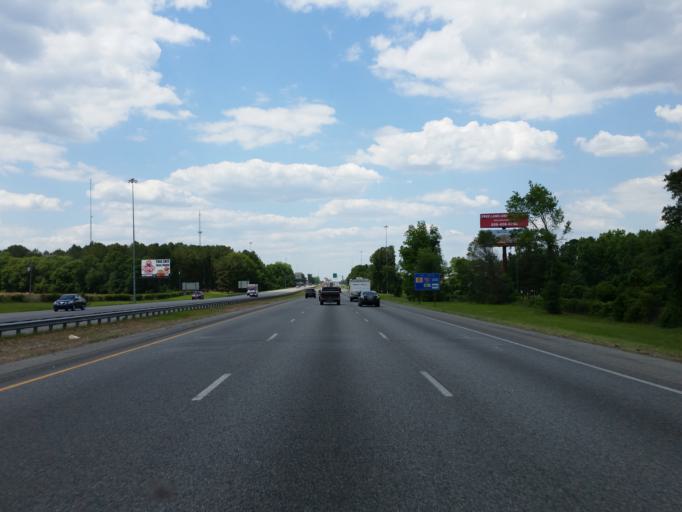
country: US
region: Georgia
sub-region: Lowndes County
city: Remerton
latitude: 30.8300
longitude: -83.3233
